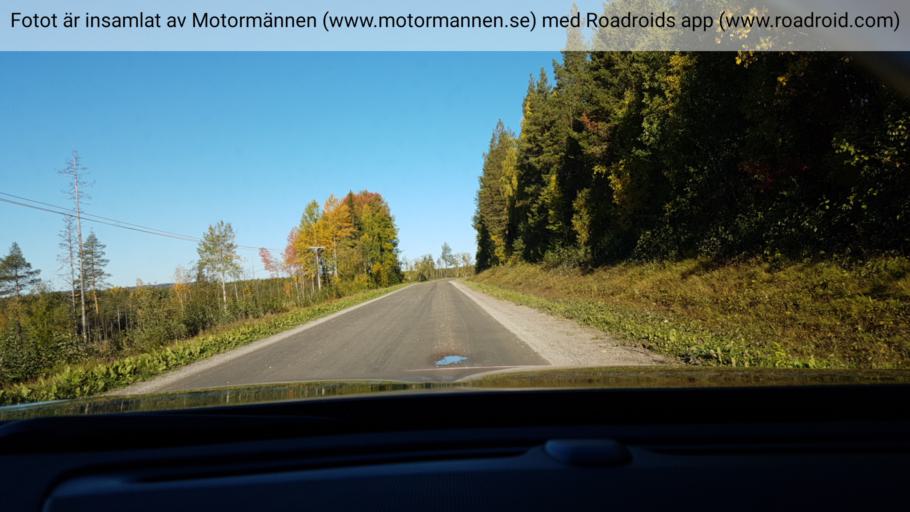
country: SE
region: Norrbotten
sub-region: Alvsbyns Kommun
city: AElvsbyn
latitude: 66.1877
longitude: 21.2041
